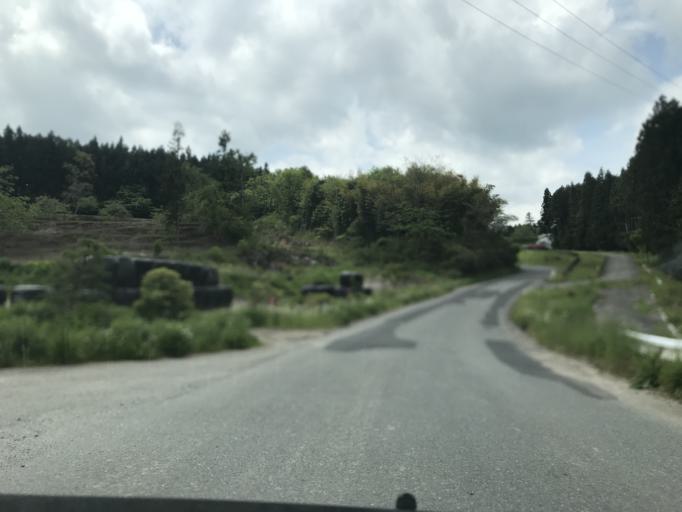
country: JP
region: Miyagi
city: Furukawa
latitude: 38.7308
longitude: 140.9276
